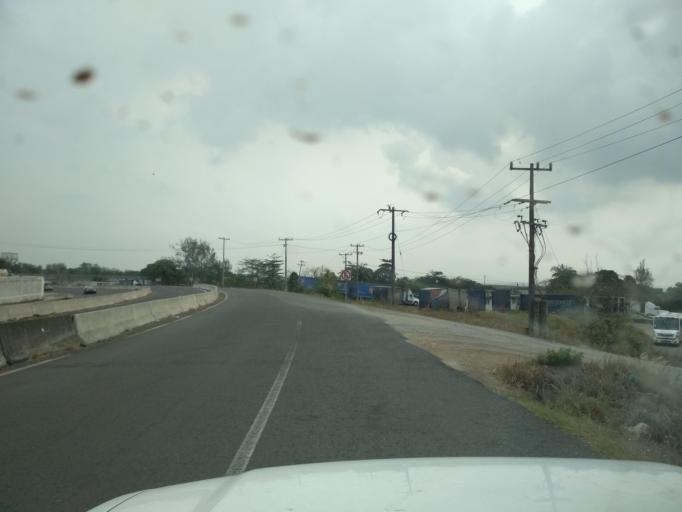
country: MX
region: Veracruz
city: Paso del Toro
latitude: 19.0196
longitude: -96.1355
